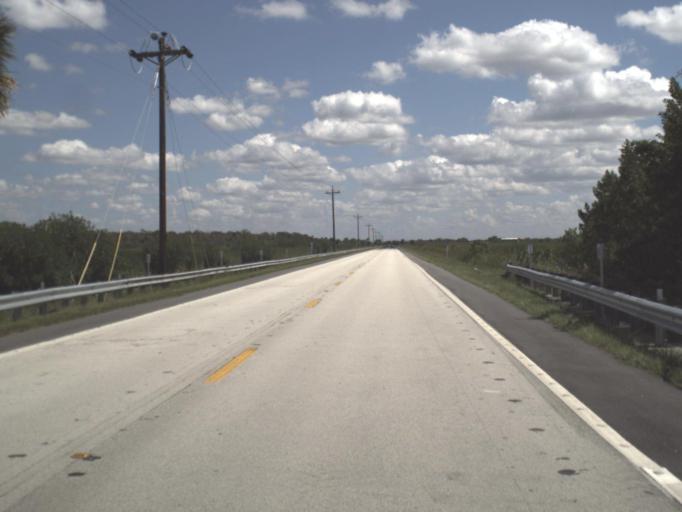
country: US
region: Florida
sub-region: Collier County
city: Marco
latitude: 25.9055
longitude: -81.3490
